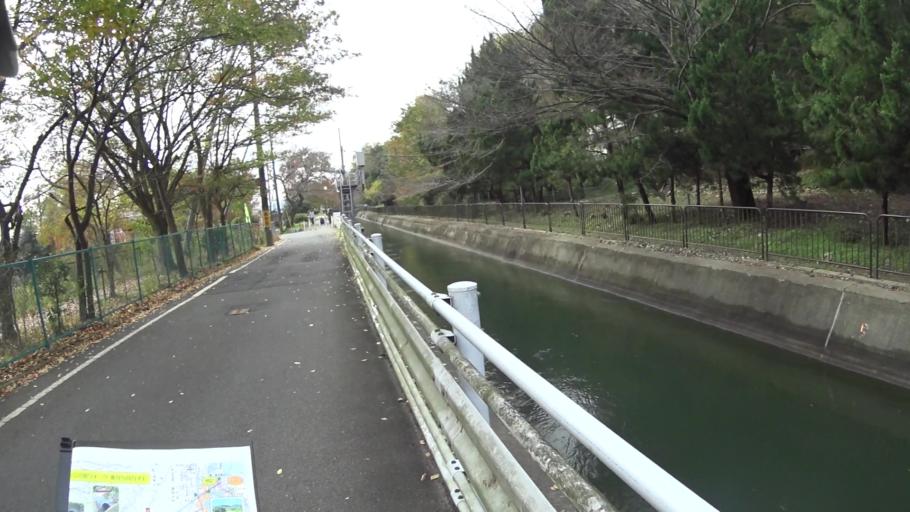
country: JP
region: Shiga Prefecture
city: Otsu-shi
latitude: 34.9961
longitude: 135.8304
